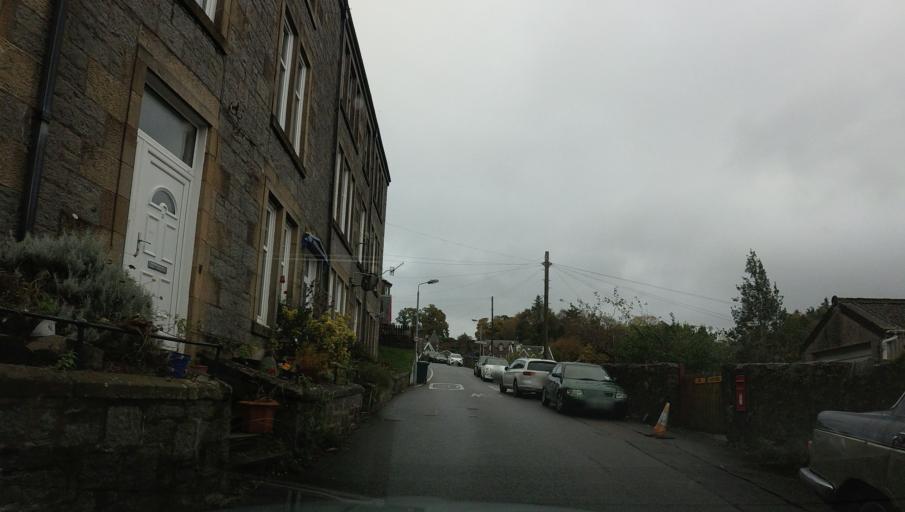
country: GB
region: Scotland
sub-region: Argyll and Bute
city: Oban
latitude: 56.4153
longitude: -5.4690
